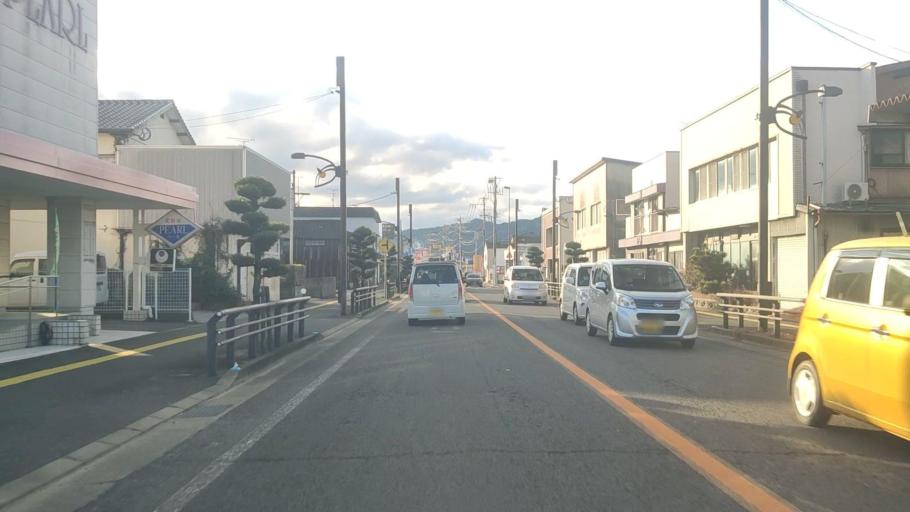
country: JP
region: Saga Prefecture
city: Saga-shi
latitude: 33.2933
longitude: 130.1946
